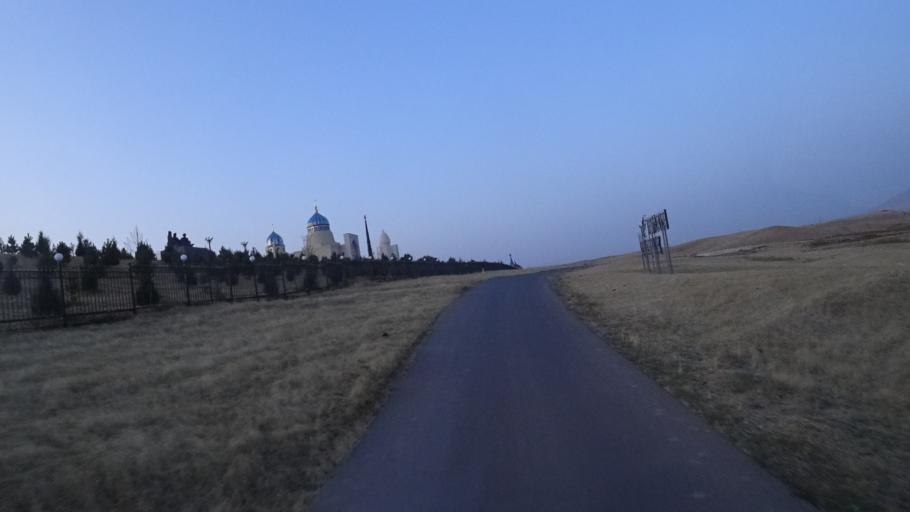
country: KZ
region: Ongtustik Qazaqstan
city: Qazyqurt
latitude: 41.8755
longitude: 69.4280
